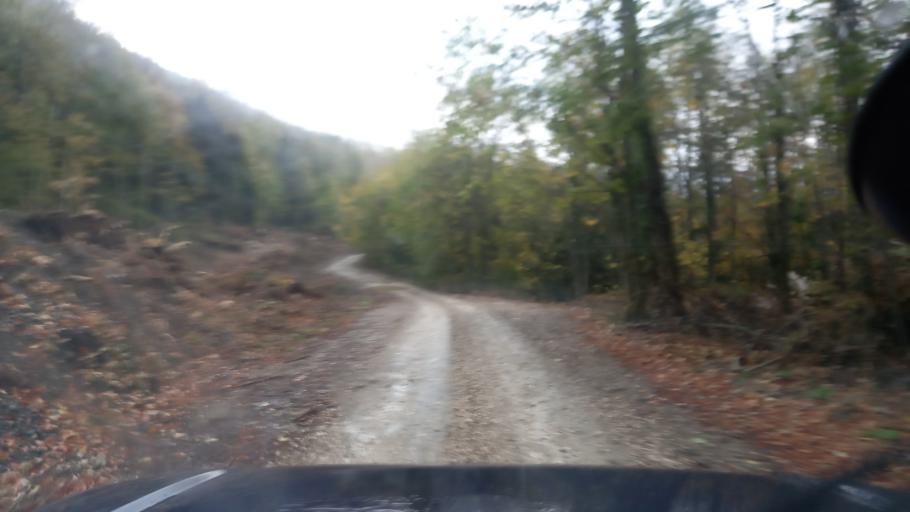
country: RU
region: Krasnodarskiy
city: Neftegorsk
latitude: 44.0470
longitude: 39.8325
